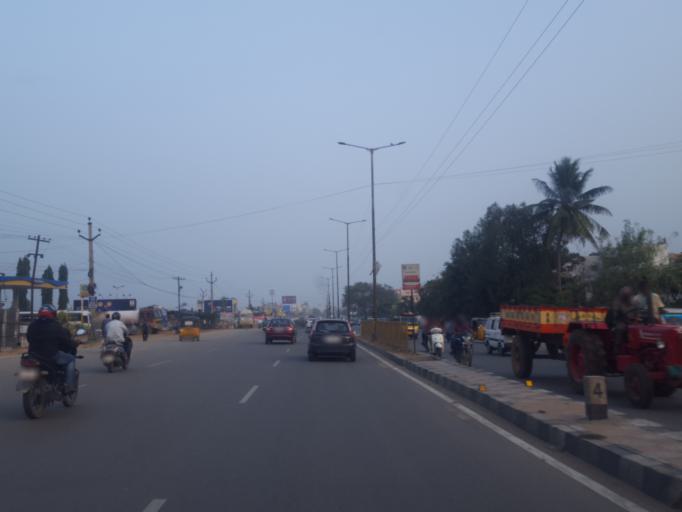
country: IN
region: Telangana
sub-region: Medak
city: Serilingampalle
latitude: 17.5131
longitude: 78.2901
